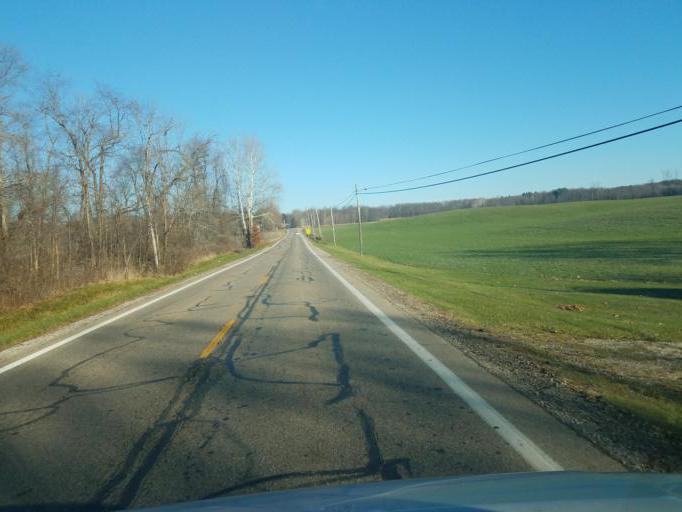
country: US
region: Ohio
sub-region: Richland County
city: Lexington
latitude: 40.6340
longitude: -82.6632
